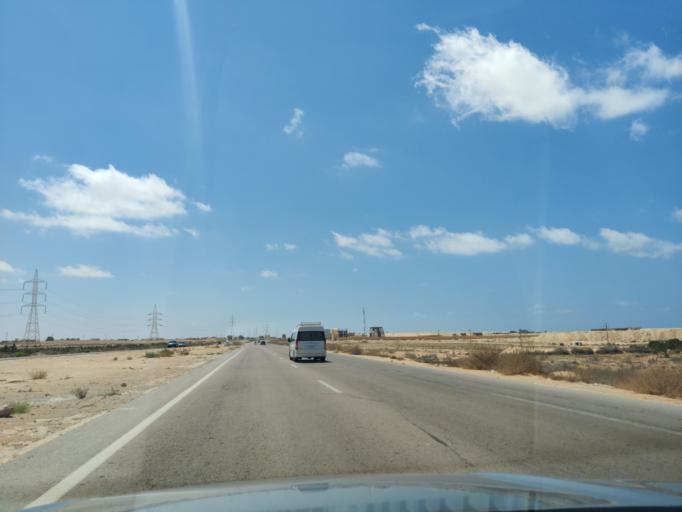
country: EG
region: Muhafazat Matruh
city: Al `Alamayn
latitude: 31.0587
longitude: 28.2111
